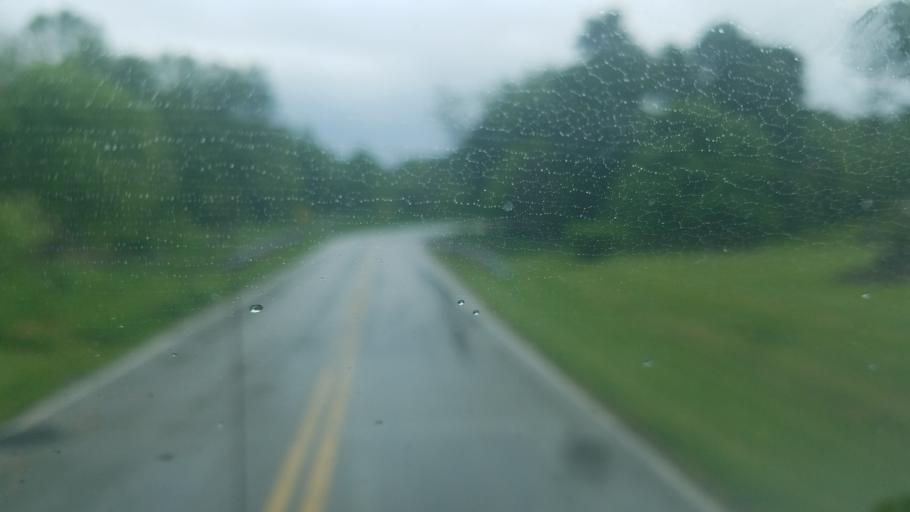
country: US
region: Ohio
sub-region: Wayne County
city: Wooster
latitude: 40.8070
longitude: -81.8887
